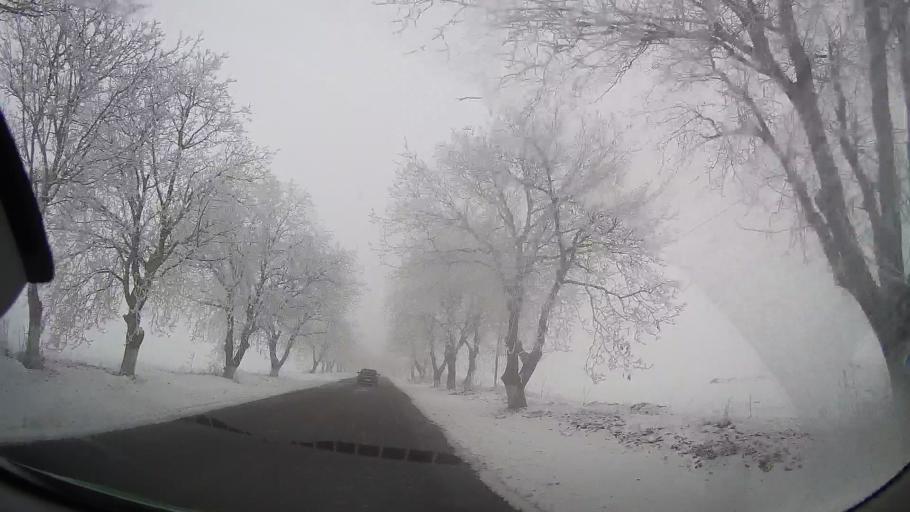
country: RO
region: Neamt
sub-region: Comuna Cordun
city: Cordun
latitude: 46.9846
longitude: 26.8644
